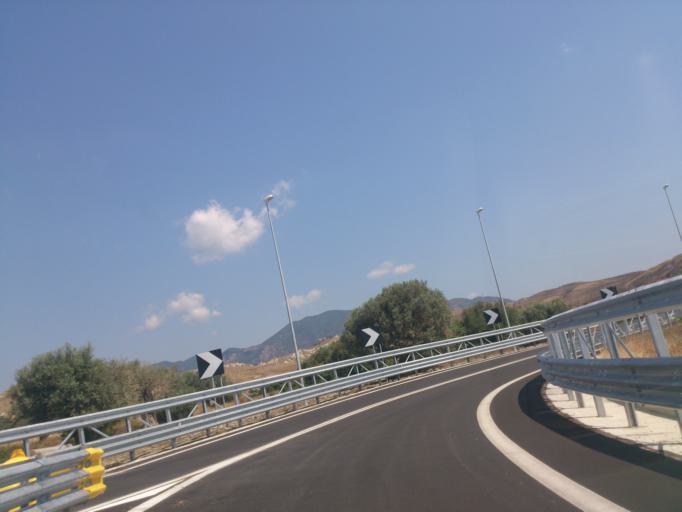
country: IT
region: Calabria
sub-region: Provincia di Reggio Calabria
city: Marina di Gioiosa Ionica
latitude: 38.3108
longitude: 16.3524
